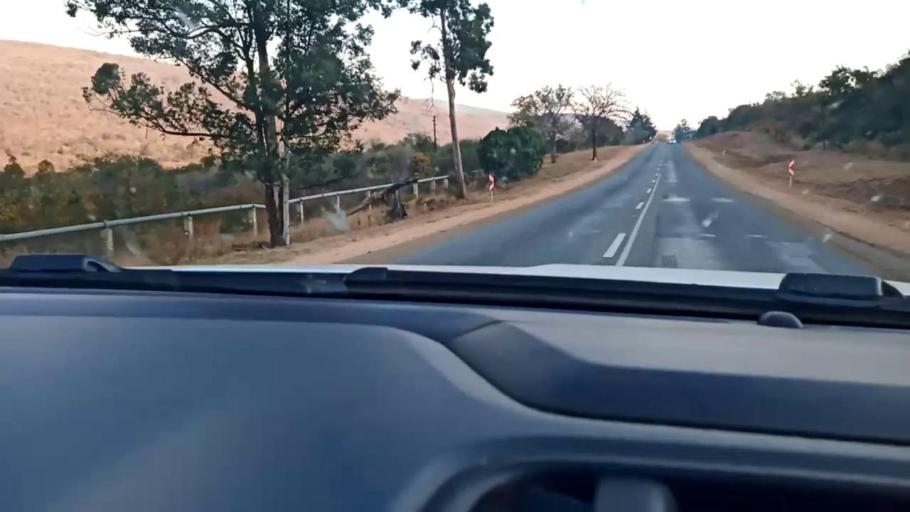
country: ZA
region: Limpopo
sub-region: Mopani District Municipality
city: Duiwelskloof
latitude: -23.6561
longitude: 30.1696
